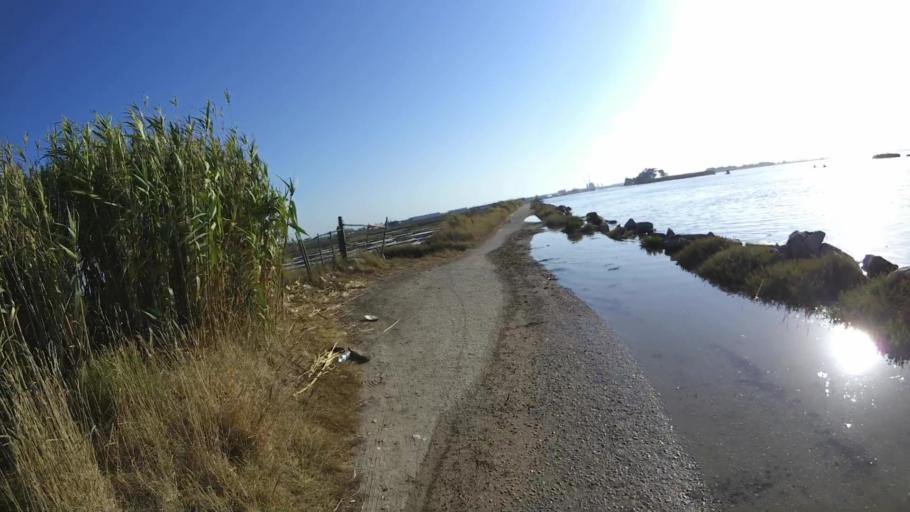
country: PT
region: Aveiro
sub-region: Aveiro
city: Aveiro
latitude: 40.6437
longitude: -8.6657
